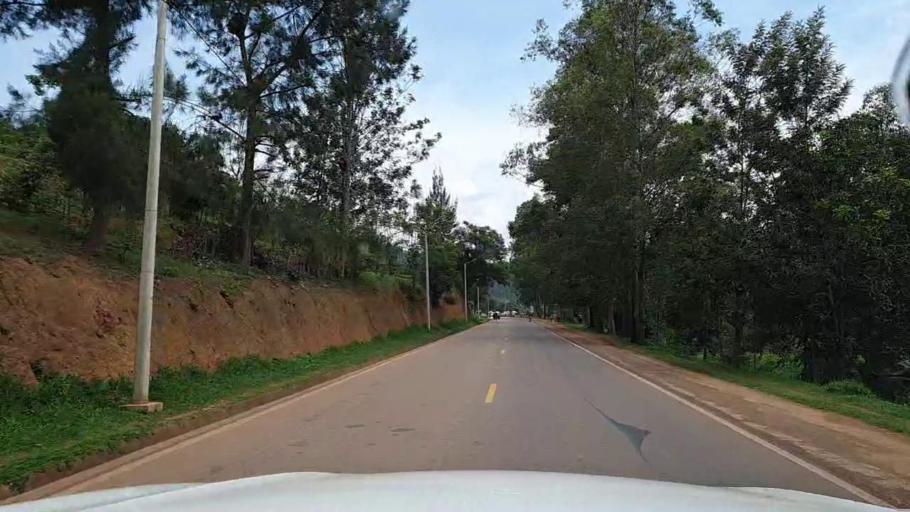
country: RW
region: Kigali
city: Kigali
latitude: -1.8688
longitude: 30.0855
